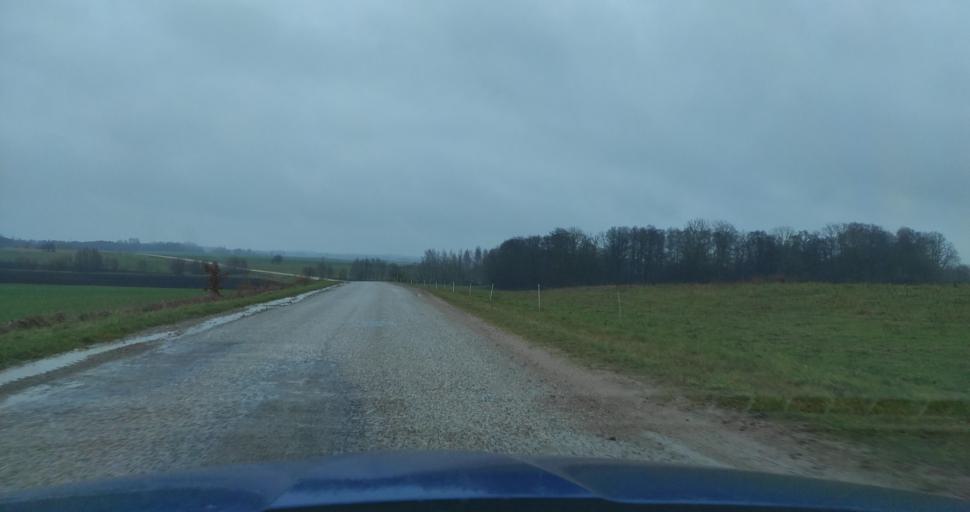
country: LV
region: Alsunga
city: Alsunga
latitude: 56.8978
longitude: 21.6128
